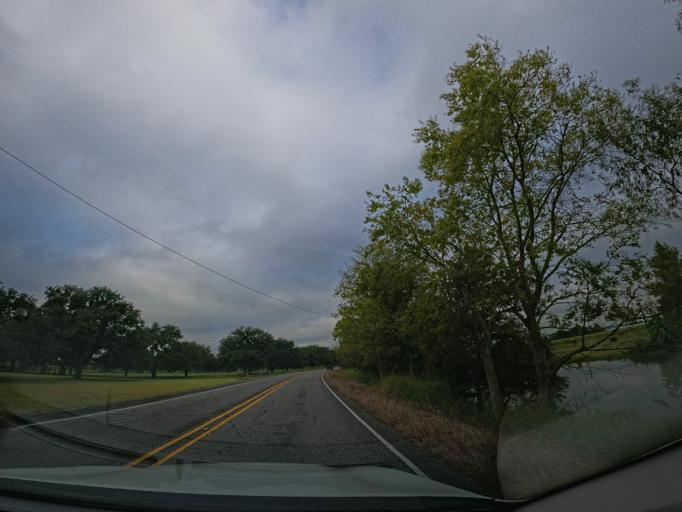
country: US
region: Louisiana
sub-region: Terrebonne Parish
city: Bayou Cane
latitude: 29.5592
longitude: -90.7880
